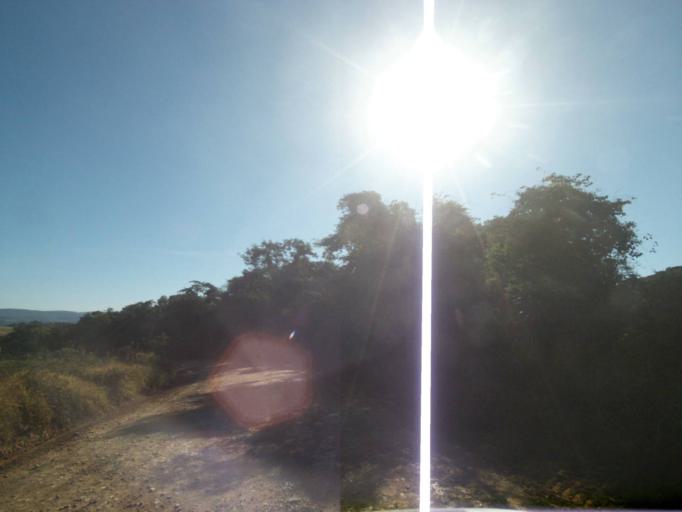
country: BR
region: Parana
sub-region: Tibagi
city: Tibagi
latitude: -24.5324
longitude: -50.4802
